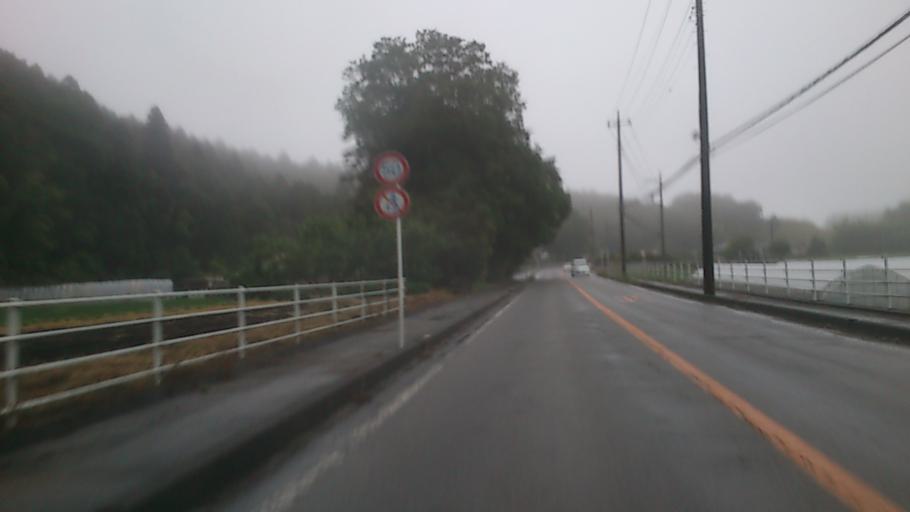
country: JP
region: Tochigi
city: Otawara
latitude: 36.8501
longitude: 140.0504
